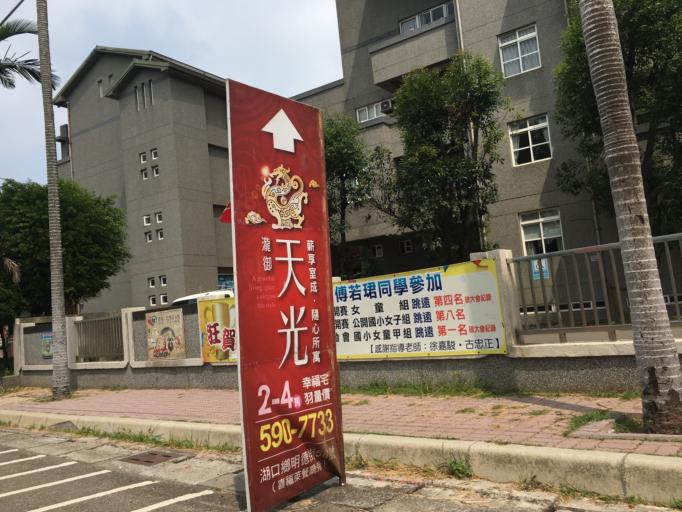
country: TW
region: Taiwan
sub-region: Hsinchu
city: Zhubei
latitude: 24.8989
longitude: 121.0386
